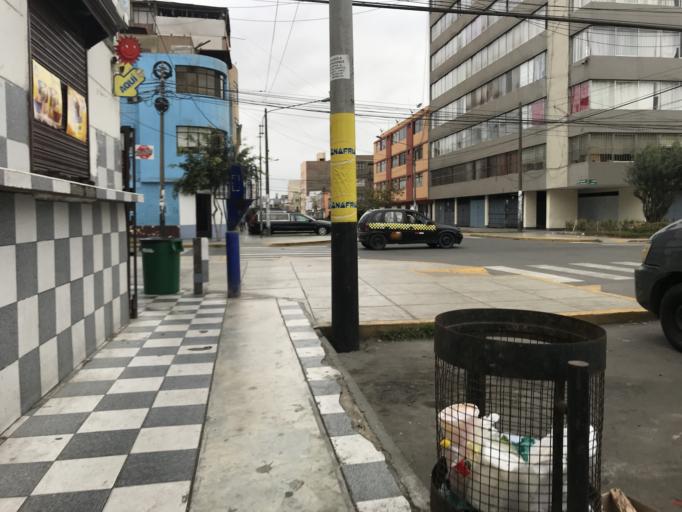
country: PE
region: Lima
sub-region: Lima
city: San Isidro
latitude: -12.0808
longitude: -77.0373
